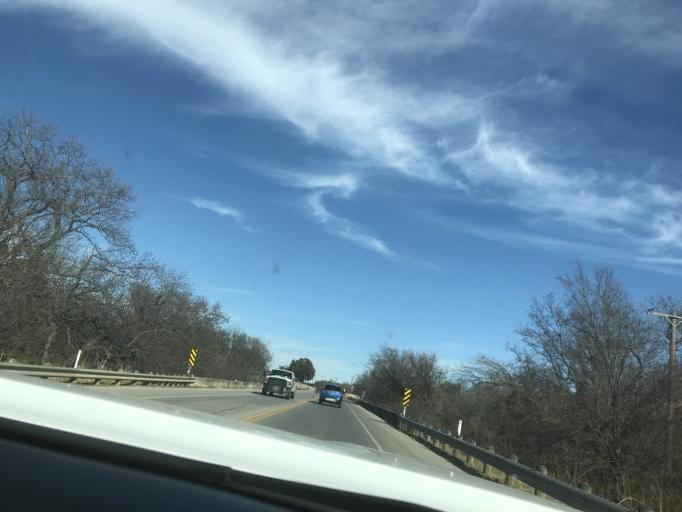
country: US
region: Texas
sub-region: Erath County
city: Stephenville
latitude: 32.2348
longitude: -98.2046
